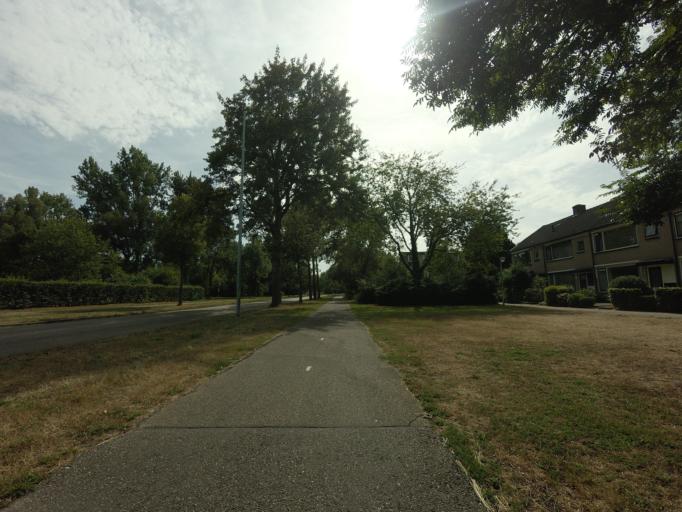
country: NL
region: Utrecht
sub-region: Gemeente Zeist
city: Zeist
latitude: 52.0870
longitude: 5.2263
